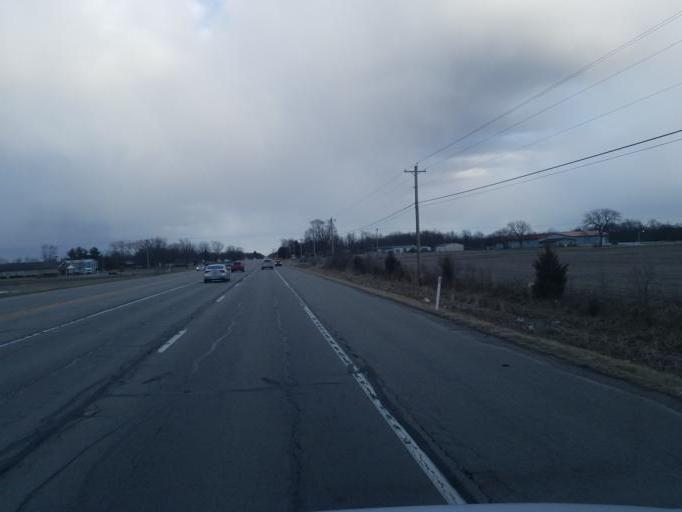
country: US
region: Indiana
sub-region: Hancock County
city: New Palestine
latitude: 39.7801
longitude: -85.8798
